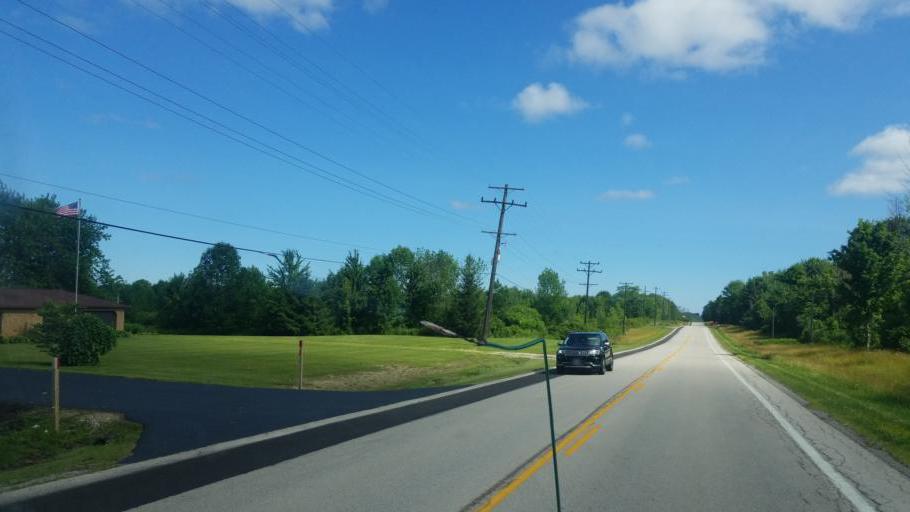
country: US
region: Ohio
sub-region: Ashtabula County
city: Conneaut
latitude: 41.8726
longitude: -80.5723
